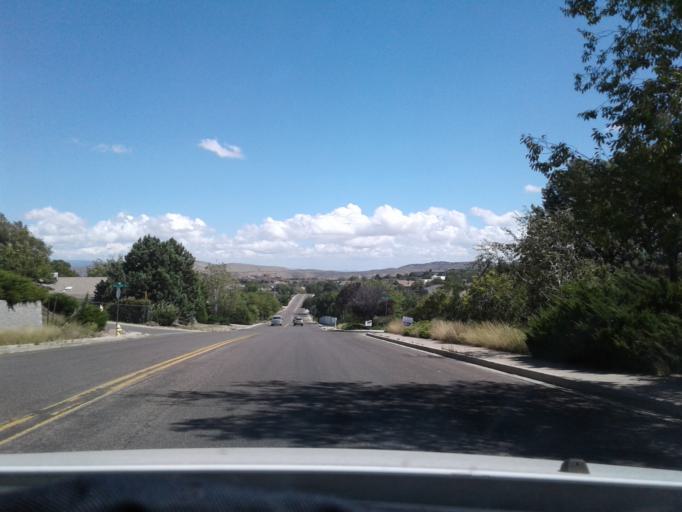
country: US
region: Arizona
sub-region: Yavapai County
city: Prescott
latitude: 34.5692
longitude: -112.4678
